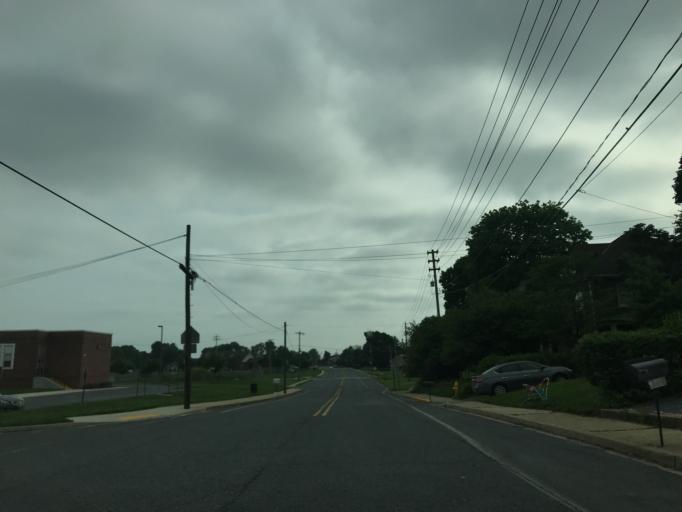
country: US
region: Maryland
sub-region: Frederick County
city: Walkersville
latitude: 39.4805
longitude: -77.3522
